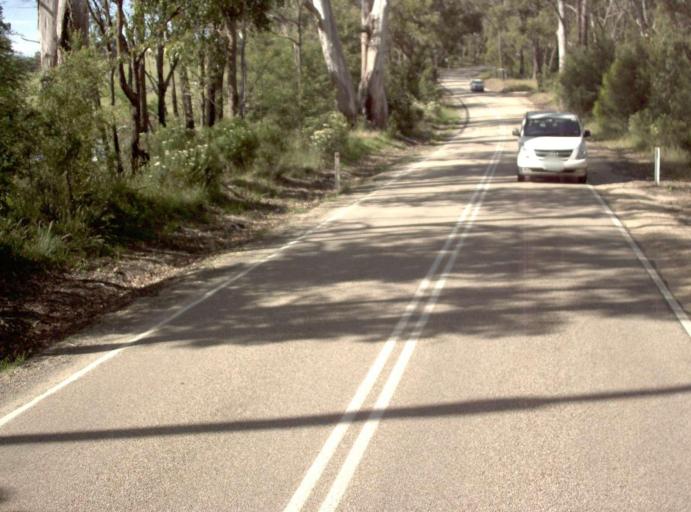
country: AU
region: Victoria
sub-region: East Gippsland
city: Lakes Entrance
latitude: -37.5231
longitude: 148.1615
